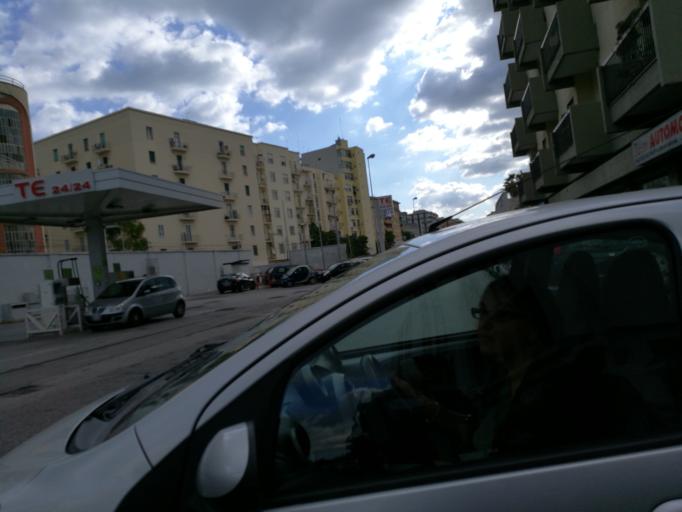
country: IT
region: Apulia
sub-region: Provincia di Bari
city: Bari
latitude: 41.1175
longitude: 16.8845
